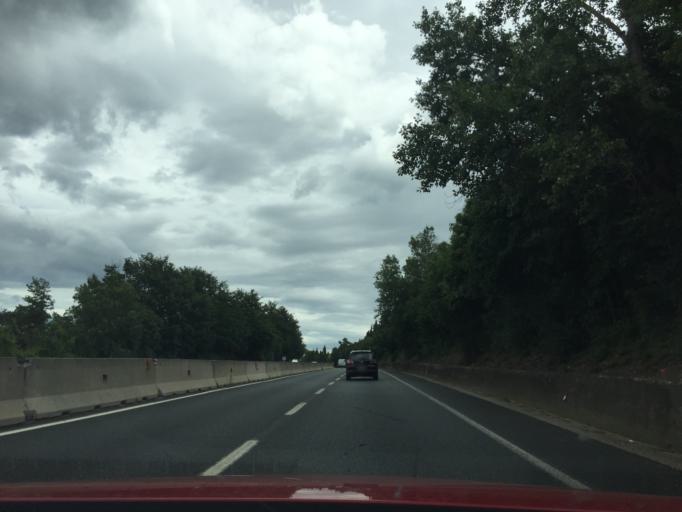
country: IT
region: Tuscany
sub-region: Province of Florence
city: Quattro Strade
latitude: 43.7282
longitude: 11.0955
